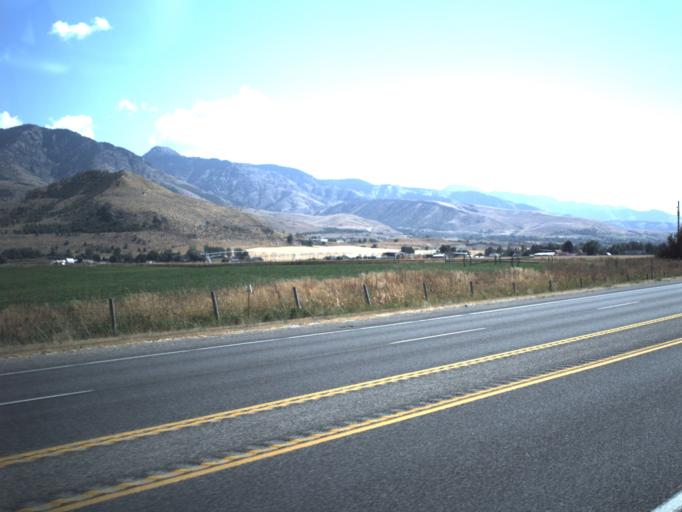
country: US
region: Utah
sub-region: Cache County
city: Lewiston
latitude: 41.9777
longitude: -111.8129
